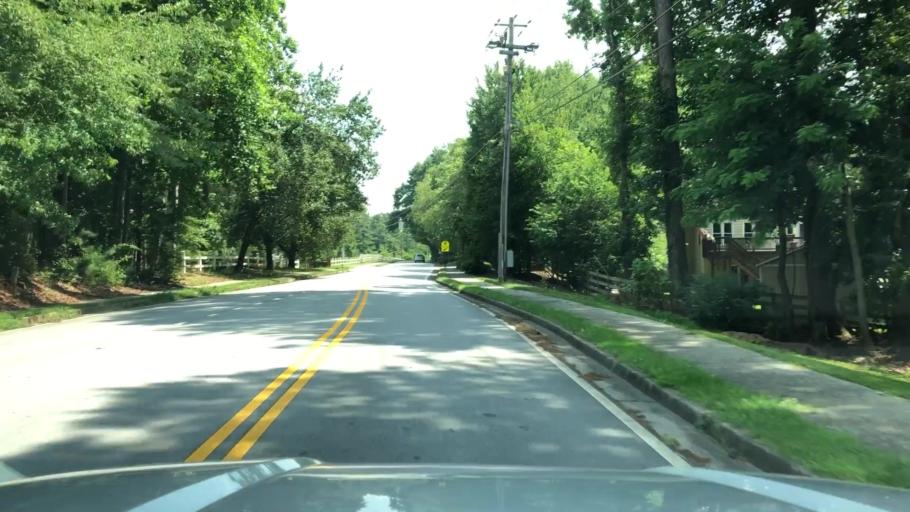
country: US
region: Georgia
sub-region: Paulding County
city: Hiram
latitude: 33.9589
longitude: -84.7258
